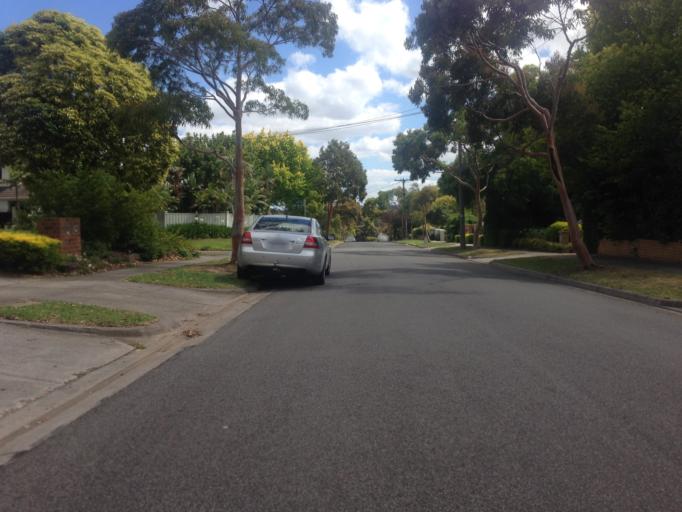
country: AU
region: Victoria
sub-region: Boroondara
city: Balwyn North
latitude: -37.7836
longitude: 145.0836
